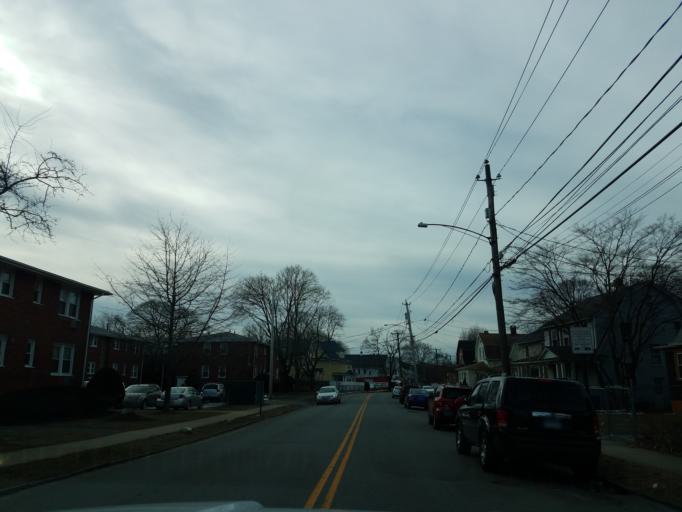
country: US
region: Connecticut
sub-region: Fairfield County
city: Trumbull
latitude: 41.2084
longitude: -73.2063
